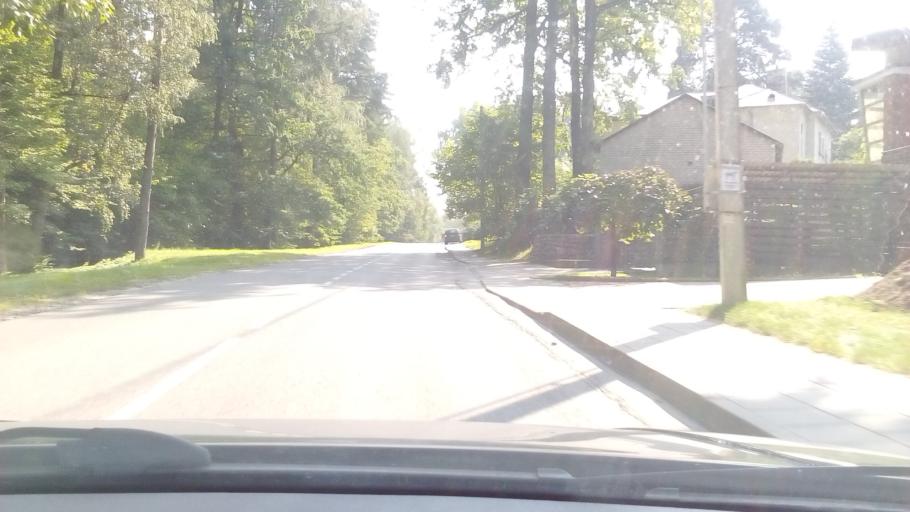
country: LT
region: Alytaus apskritis
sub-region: Alytus
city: Alytus
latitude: 54.3924
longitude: 24.0587
